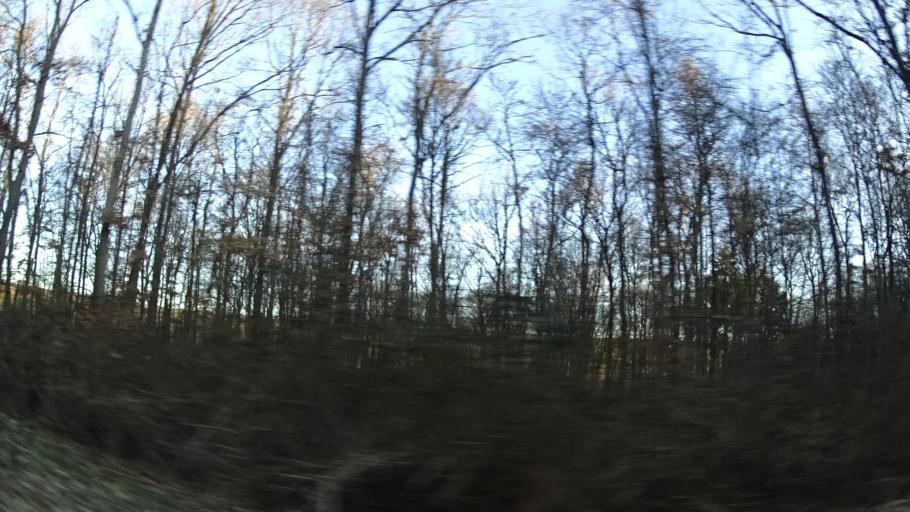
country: DE
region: Rheinland-Pfalz
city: Bennhausen
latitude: 49.6401
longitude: 7.9809
